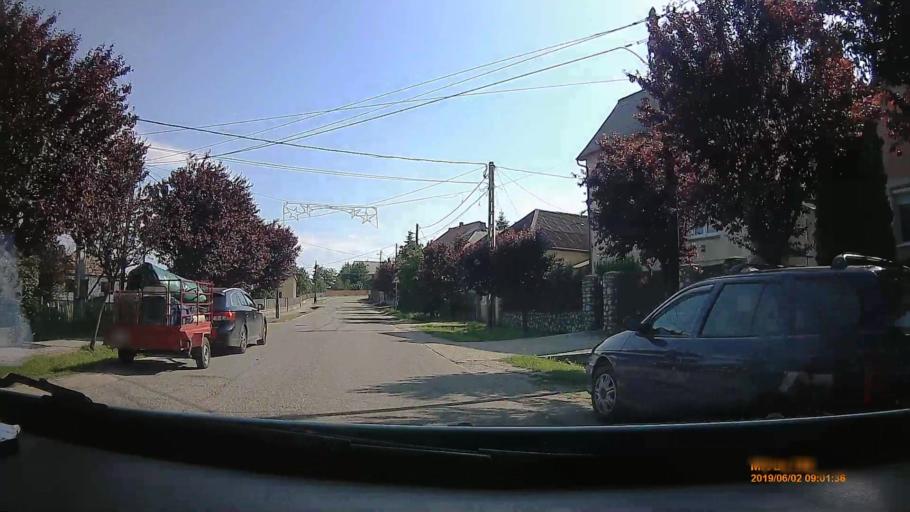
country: HU
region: Borsod-Abauj-Zemplen
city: Kazincbarcika
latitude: 48.1642
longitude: 20.6254
